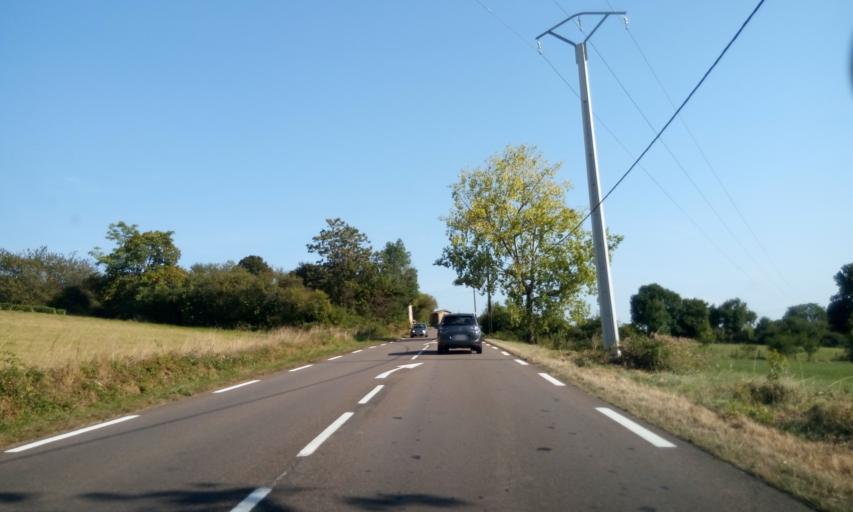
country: FR
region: Rhone-Alpes
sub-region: Departement du Rhone
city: Theize
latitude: 45.9129
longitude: 4.6000
